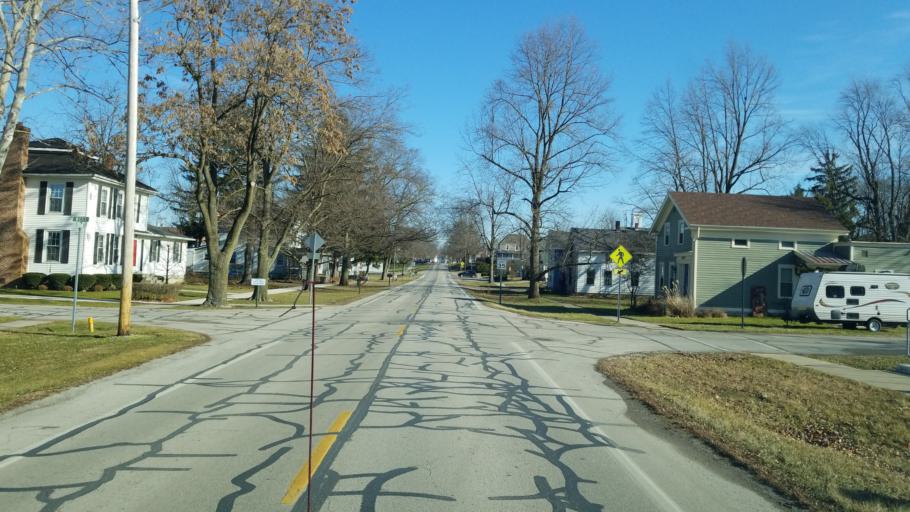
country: US
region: Ohio
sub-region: Wood County
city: Weston
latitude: 41.4108
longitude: -83.8704
